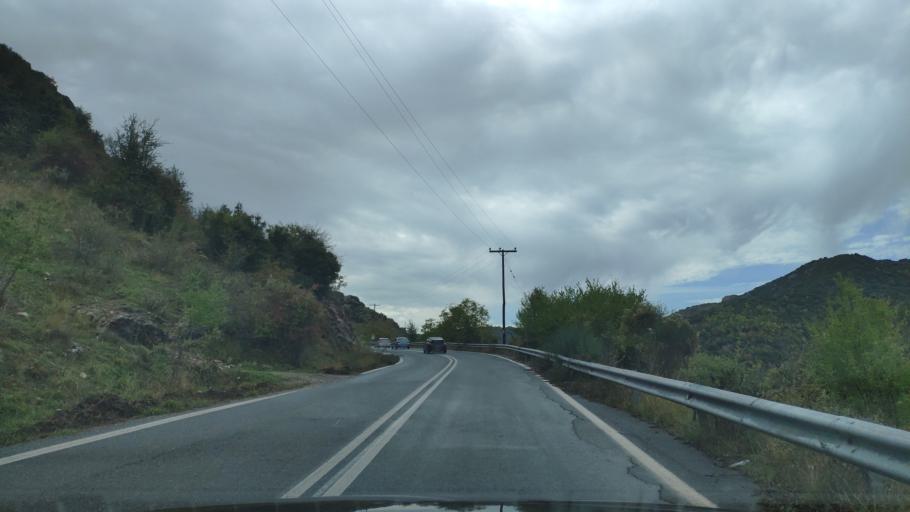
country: GR
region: Peloponnese
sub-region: Nomos Arkadias
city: Dimitsana
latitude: 37.6101
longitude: 22.0423
